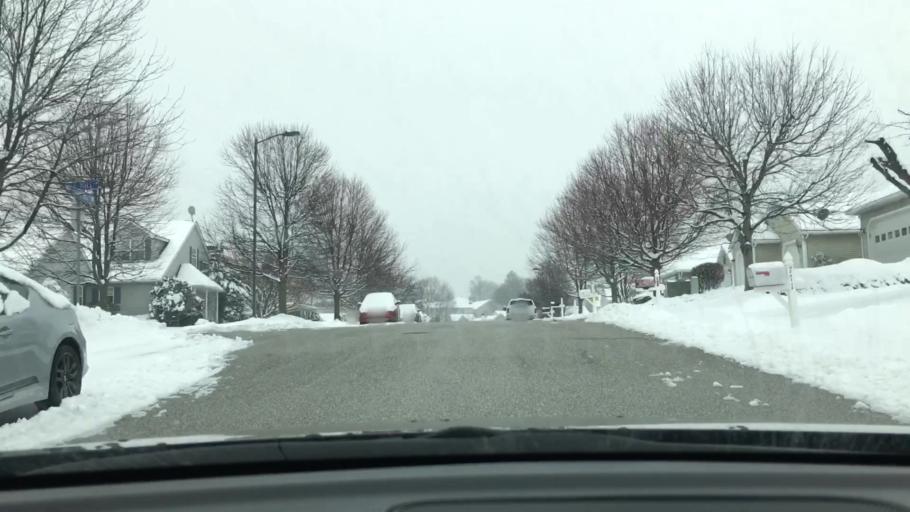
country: US
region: Pennsylvania
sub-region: York County
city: Yoe
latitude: 39.9096
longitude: -76.6496
